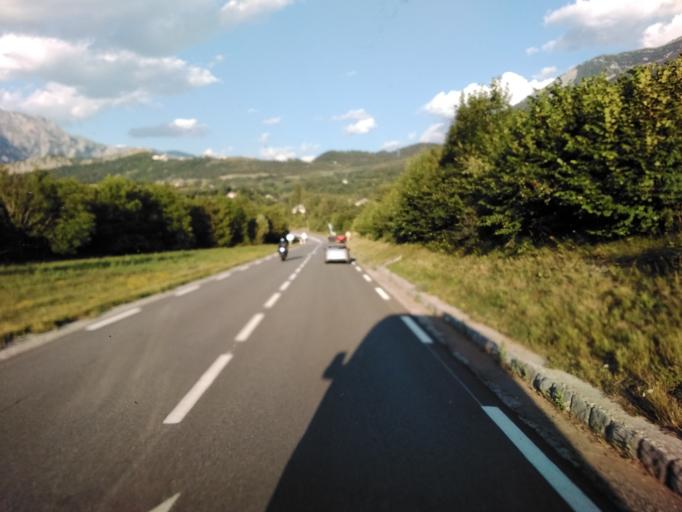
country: FR
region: Provence-Alpes-Cote d'Azur
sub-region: Departement des Alpes-de-Haute-Provence
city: Seyne-les-Alpes
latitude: 44.4435
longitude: 6.3465
